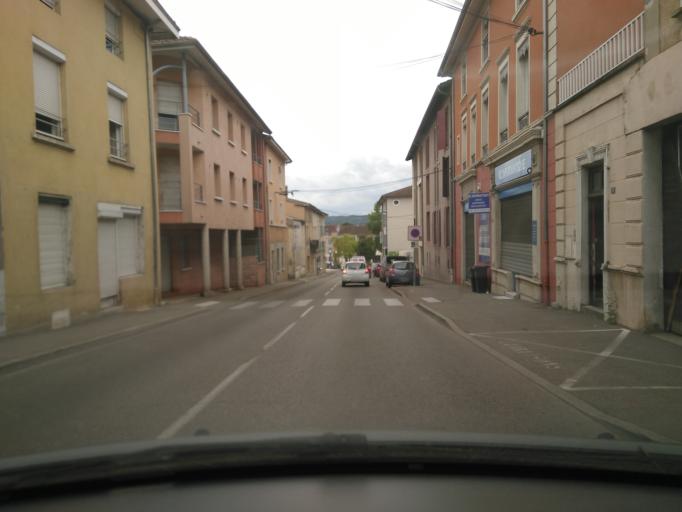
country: FR
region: Rhone-Alpes
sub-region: Departement de l'Isere
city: Beaurepaire
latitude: 45.3394
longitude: 5.0529
